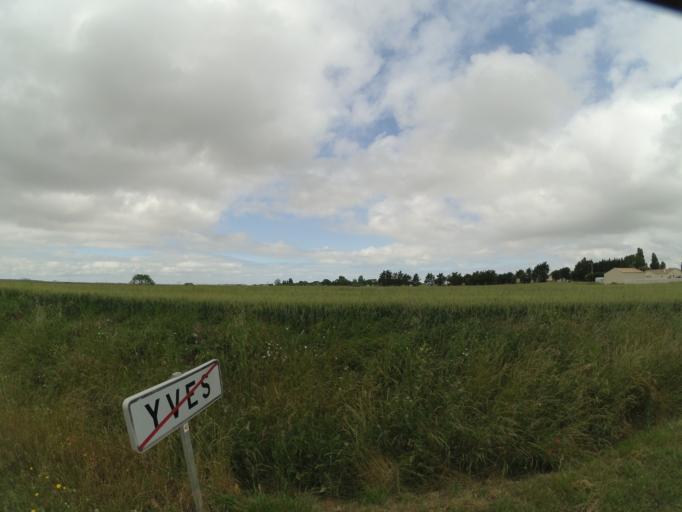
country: FR
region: Poitou-Charentes
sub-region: Departement de la Charente-Maritime
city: Yves
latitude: 46.0164
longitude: -1.0491
